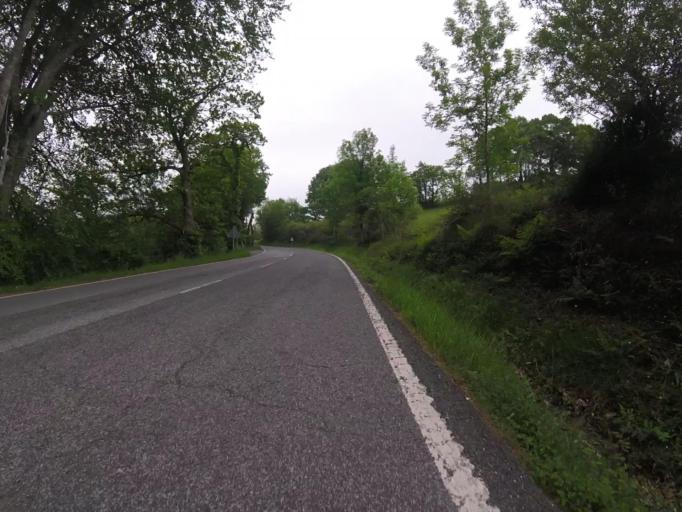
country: ES
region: Navarre
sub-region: Provincia de Navarra
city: Zugarramurdi
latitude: 43.2642
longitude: -1.4903
